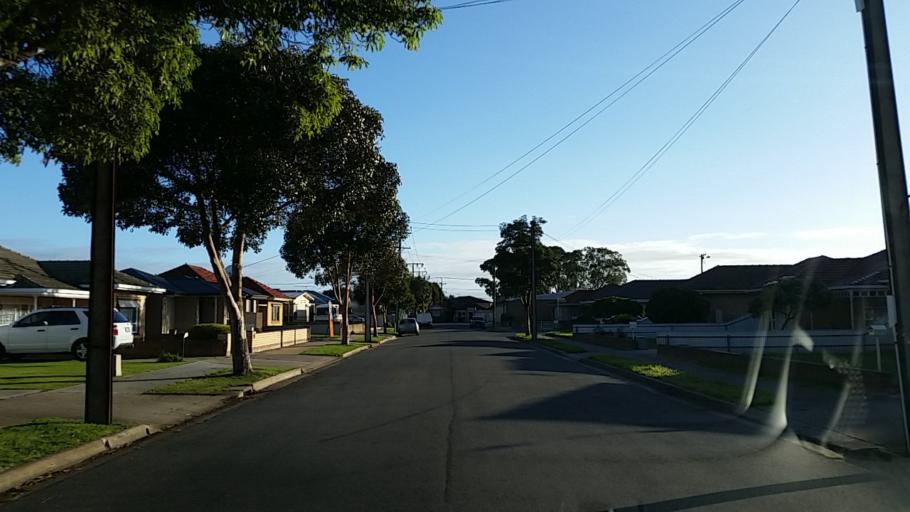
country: AU
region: South Australia
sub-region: Charles Sturt
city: Findon
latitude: -34.8963
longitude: 138.5365
